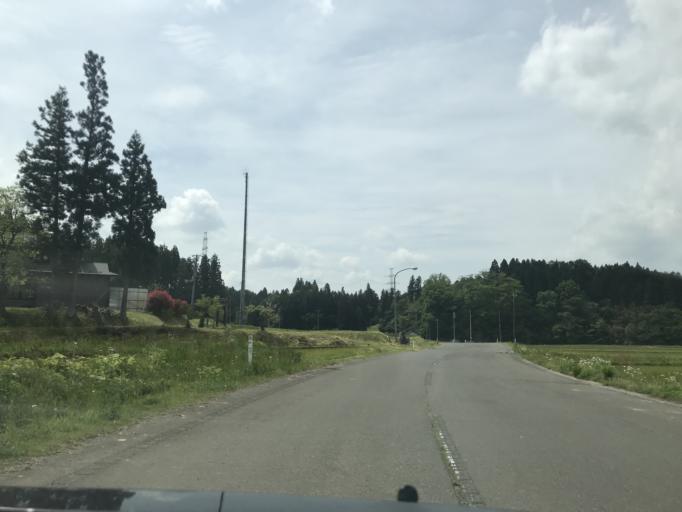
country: JP
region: Iwate
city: Ichinoseki
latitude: 38.8682
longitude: 140.9810
